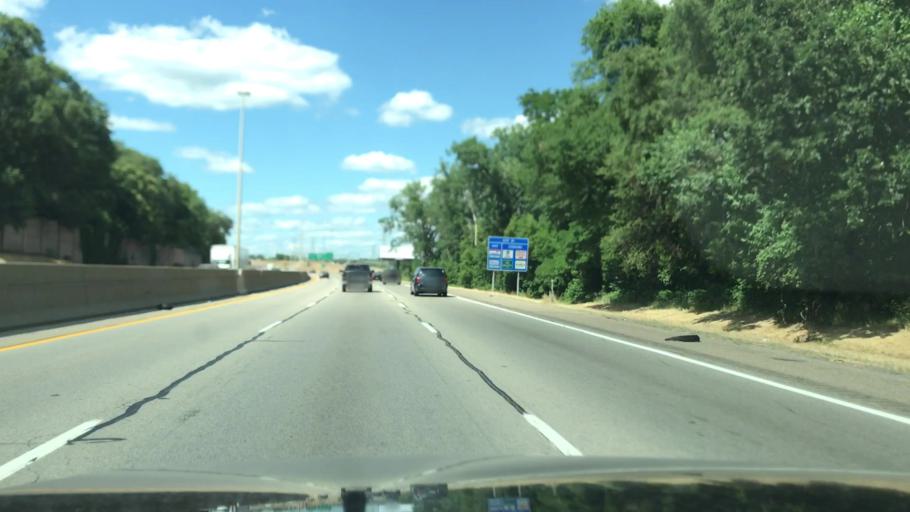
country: US
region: Michigan
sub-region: Kent County
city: Wyoming
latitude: 42.9064
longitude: -85.6769
